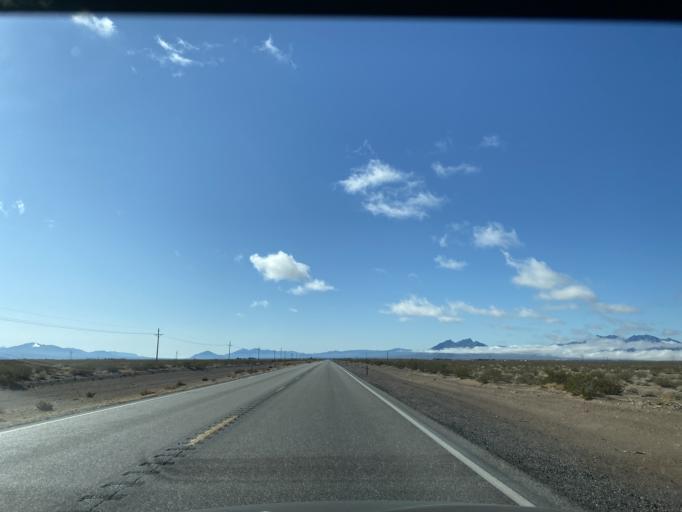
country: US
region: Nevada
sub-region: Nye County
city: Beatty
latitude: 36.5481
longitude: -116.4170
